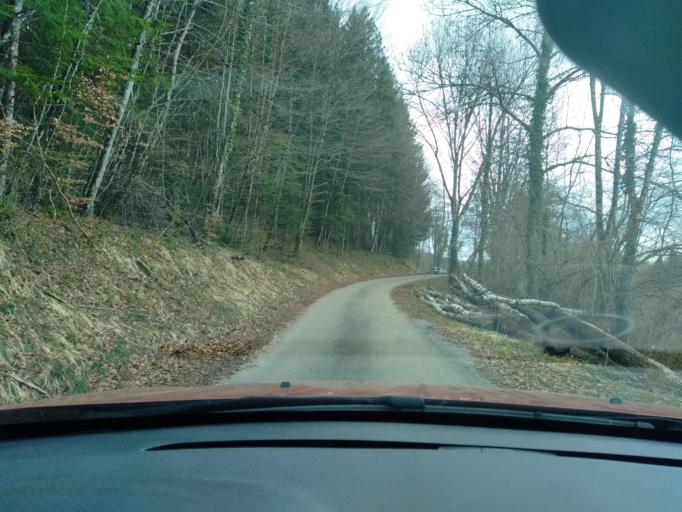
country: FR
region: Franche-Comte
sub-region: Departement du Jura
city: Moirans-en-Montagne
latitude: 46.4596
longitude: 5.7607
